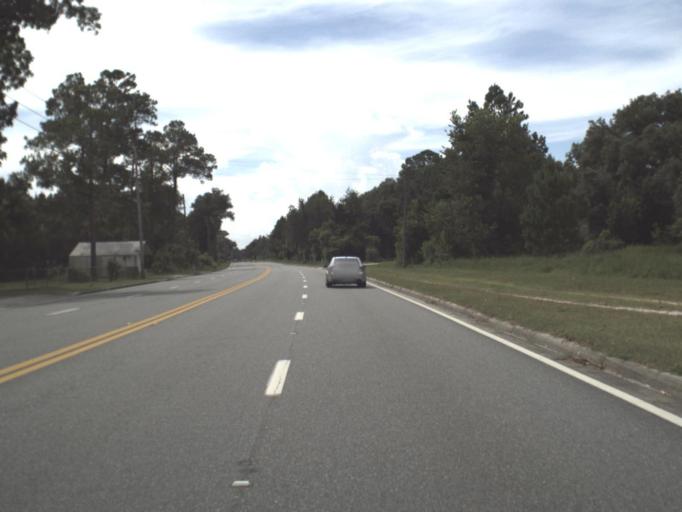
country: US
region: Florida
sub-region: Taylor County
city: Perry
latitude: 30.0884
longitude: -83.5319
